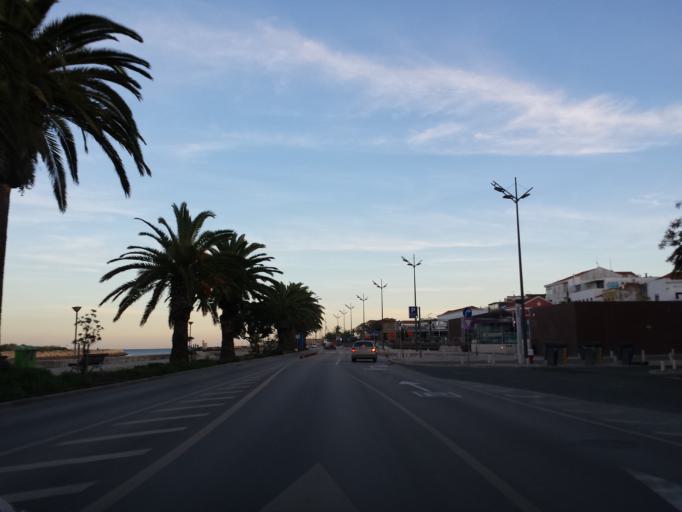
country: PT
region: Faro
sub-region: Lagos
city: Lagos
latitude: 37.1028
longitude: -8.6718
